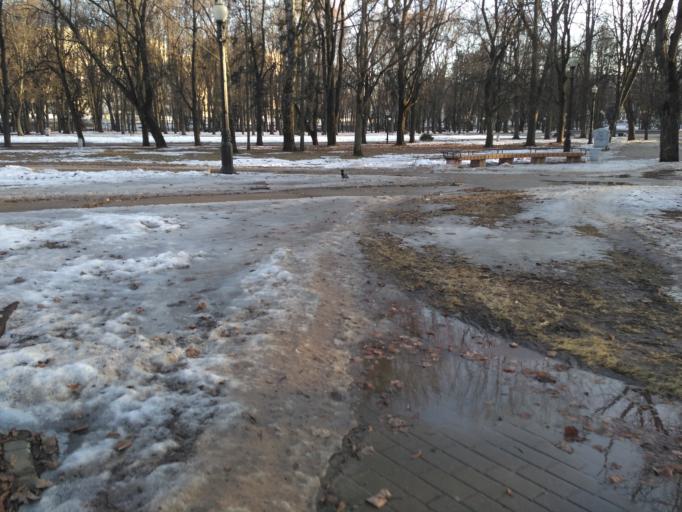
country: BY
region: Minsk
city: Minsk
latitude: 53.9077
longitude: 27.5670
